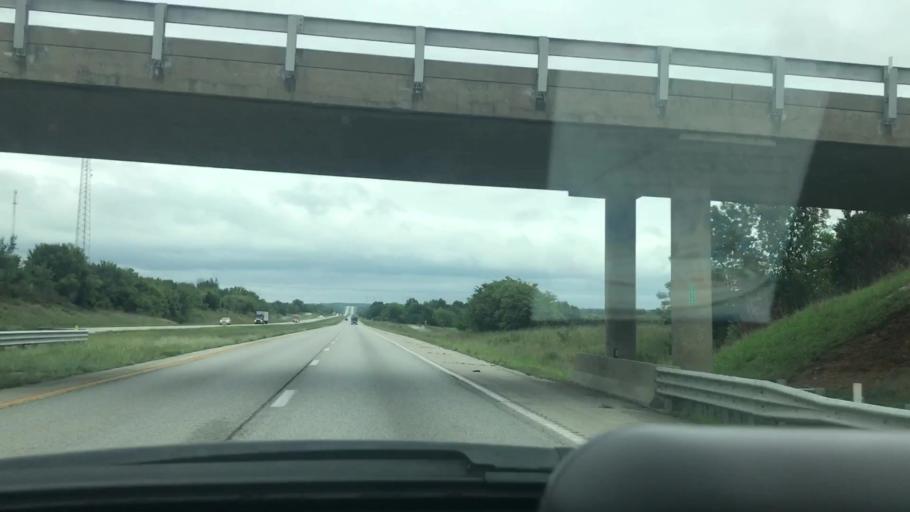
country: US
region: Missouri
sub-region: Lawrence County
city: Mount Vernon
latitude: 37.1547
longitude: -93.6963
